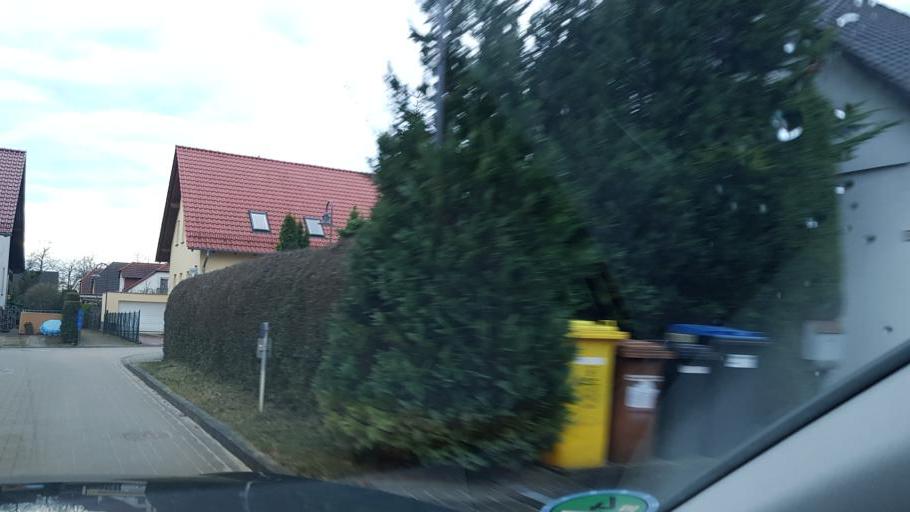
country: DE
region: Brandenburg
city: Frankfurt (Oder)
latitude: 52.3278
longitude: 14.5024
